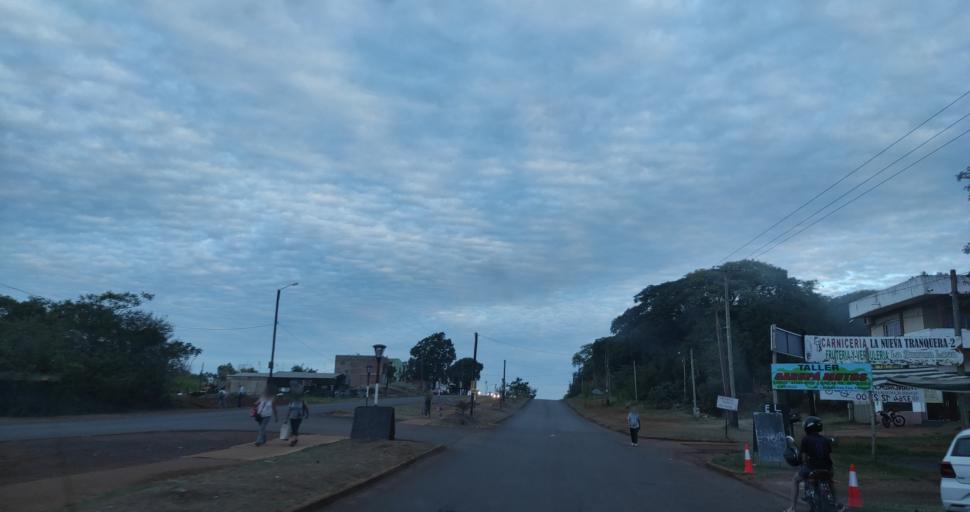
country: AR
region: Misiones
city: Garupa
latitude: -27.4668
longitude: -55.8536
